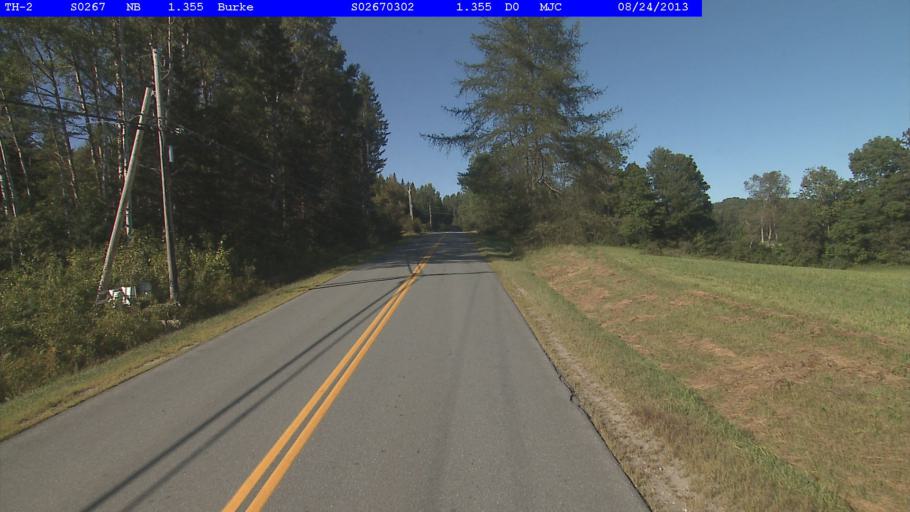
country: US
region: Vermont
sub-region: Caledonia County
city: Lyndonville
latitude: 44.6057
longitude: -71.9381
